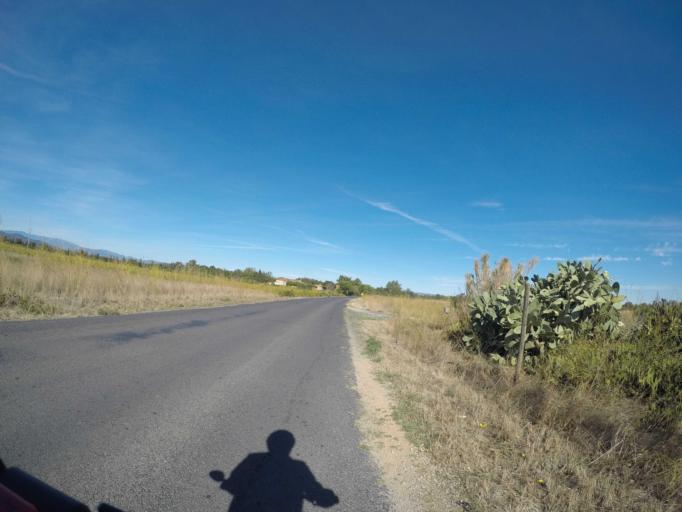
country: FR
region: Languedoc-Roussillon
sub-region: Departement des Pyrenees-Orientales
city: Ponteilla
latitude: 42.6482
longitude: 2.7995
